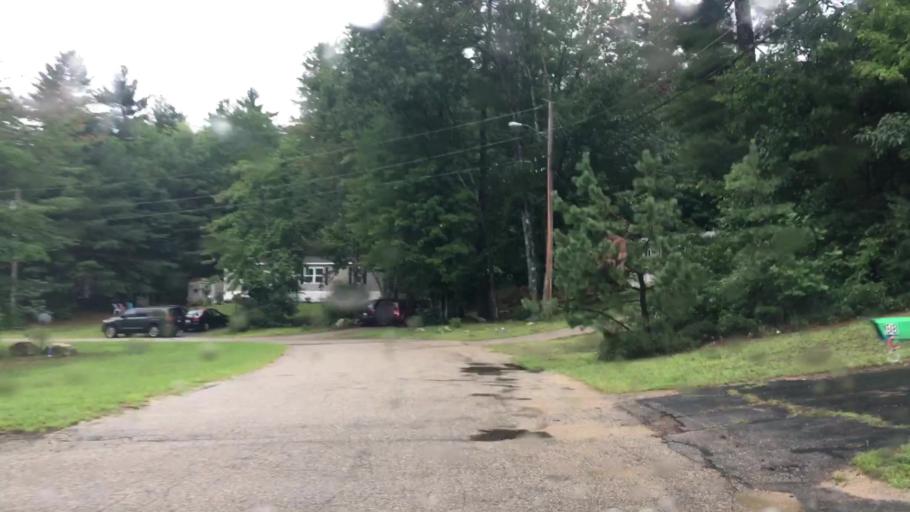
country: US
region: New Hampshire
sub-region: Carroll County
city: Conway
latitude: 43.9949
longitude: -71.0994
